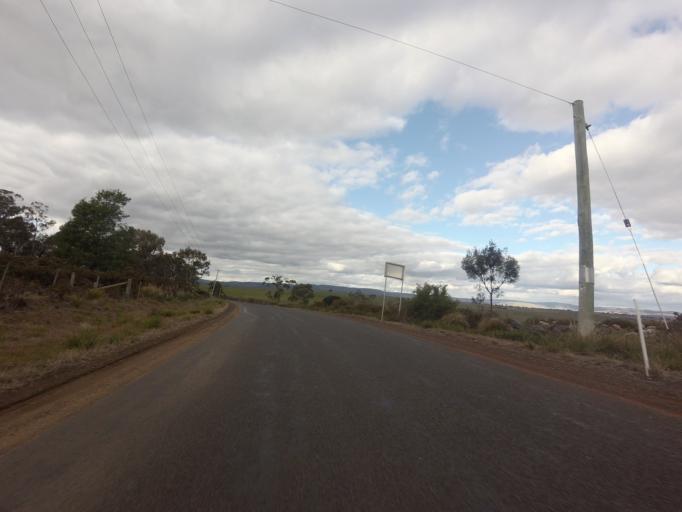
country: AU
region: Tasmania
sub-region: Northern Midlands
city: Evandale
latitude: -41.8946
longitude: 147.4120
